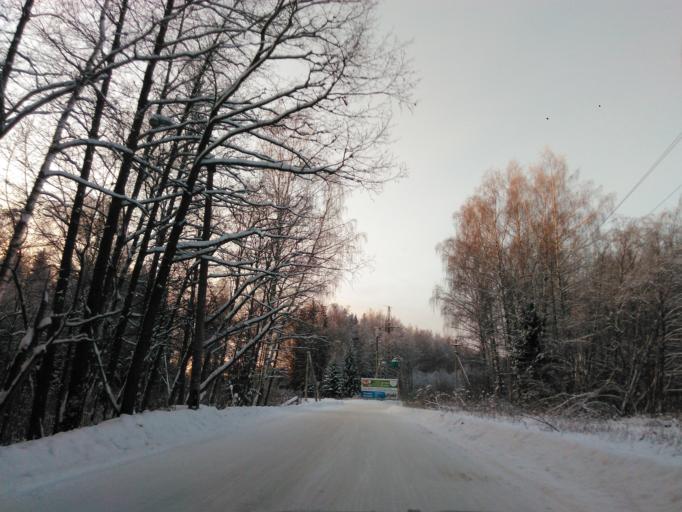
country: RU
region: Tverskaya
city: Konakovo
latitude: 56.6664
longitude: 36.6860
